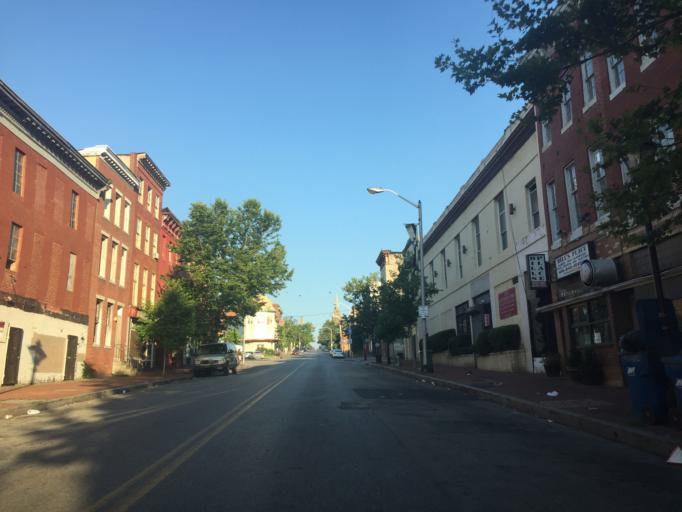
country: US
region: Maryland
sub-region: City of Baltimore
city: Baltimore
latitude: 39.2885
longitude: -76.6413
